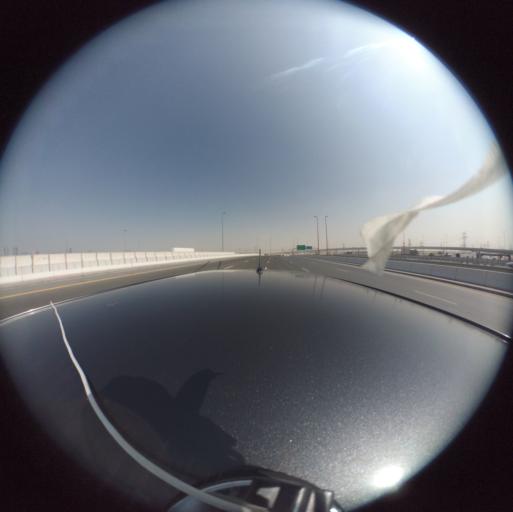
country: AE
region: Dubai
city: Dubai
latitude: 25.1442
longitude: 55.2577
